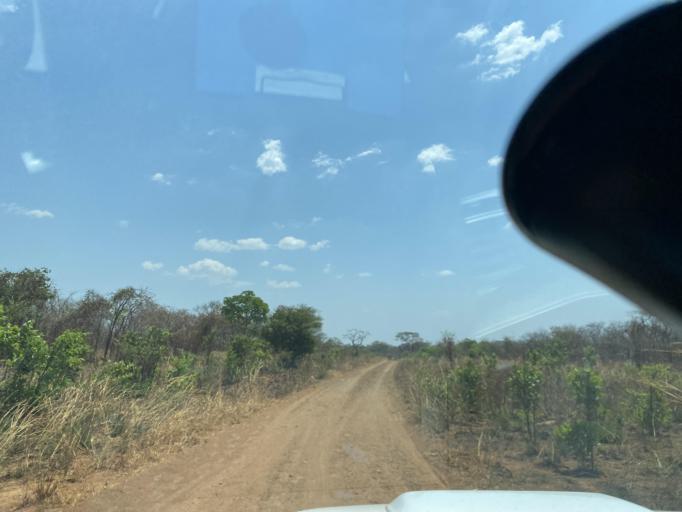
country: ZM
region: Lusaka
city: Lusaka
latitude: -15.5085
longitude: 28.0047
